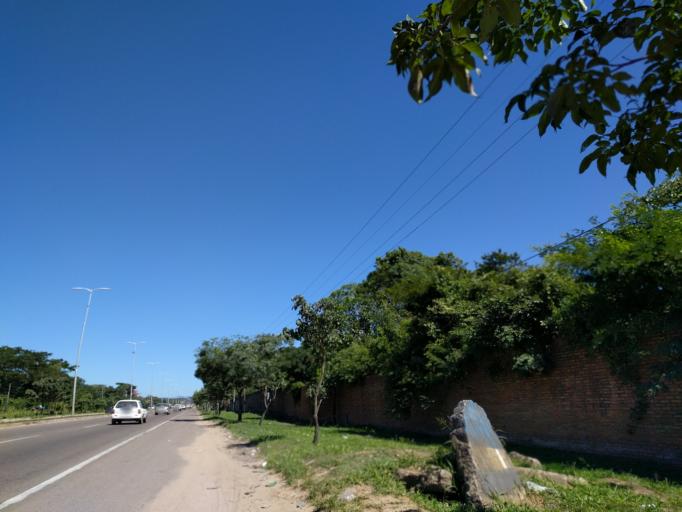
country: BO
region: Santa Cruz
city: Santa Rita
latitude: -17.8713
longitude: -63.2755
